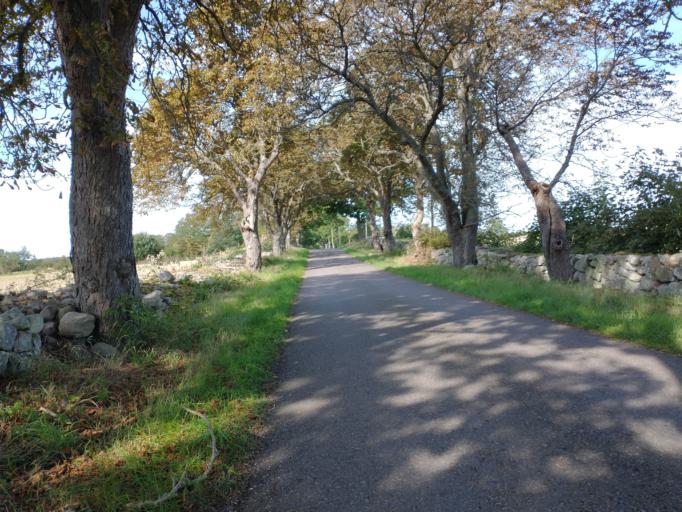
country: SE
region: Kalmar
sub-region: Kalmar Kommun
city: Lindsdal
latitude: 56.7770
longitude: 16.3208
